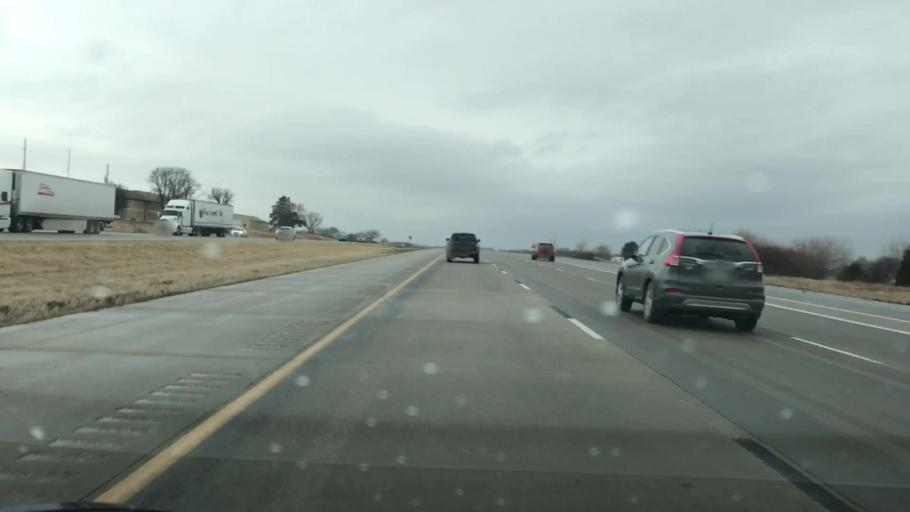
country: US
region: Nebraska
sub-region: Saunders County
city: Ashland
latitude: 40.9697
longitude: -96.3922
